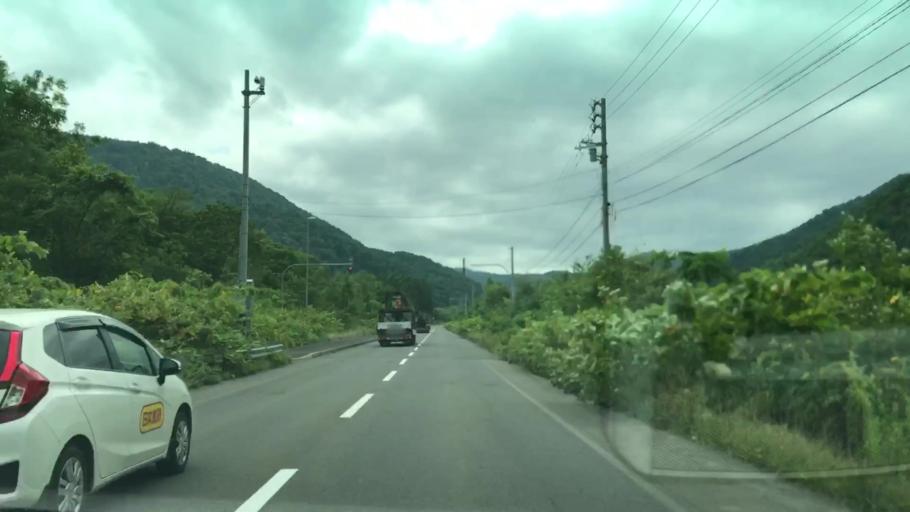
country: JP
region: Hokkaido
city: Yoichi
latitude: 43.0337
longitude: 140.8642
